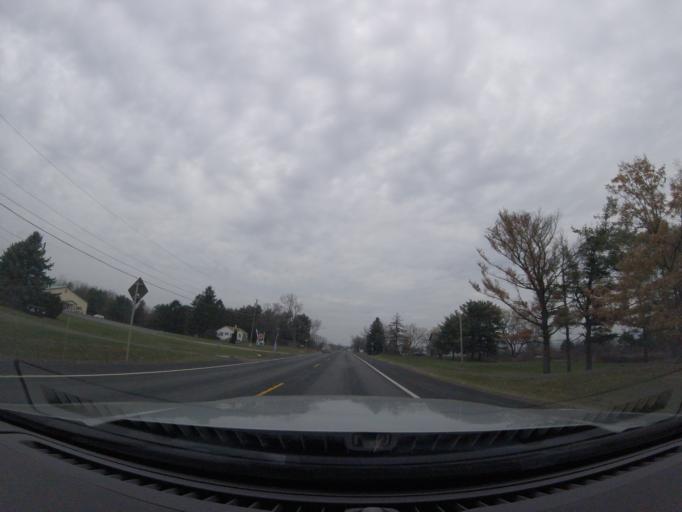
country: US
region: New York
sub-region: Schuyler County
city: Watkins Glen
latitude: 42.4505
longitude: -76.9089
